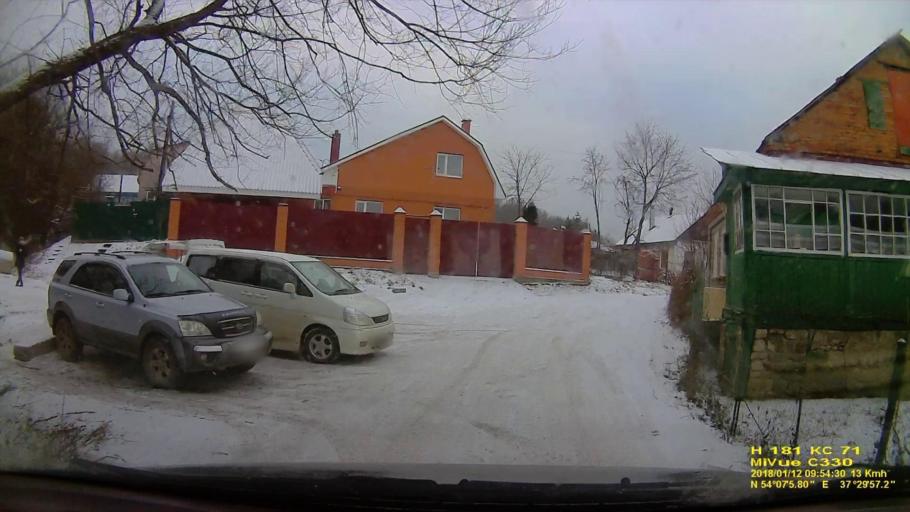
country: RU
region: Tula
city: Kosaya Gora
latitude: 54.1183
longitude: 37.4992
